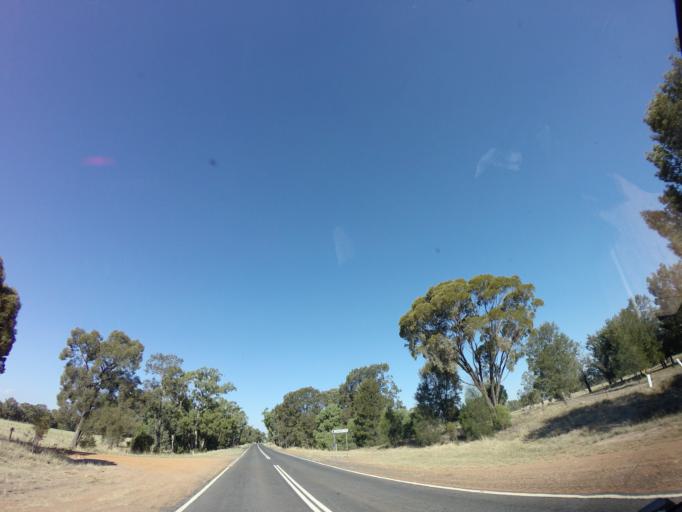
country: AU
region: New South Wales
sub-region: Gilgandra
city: Gilgandra
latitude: -31.6621
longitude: 148.4035
